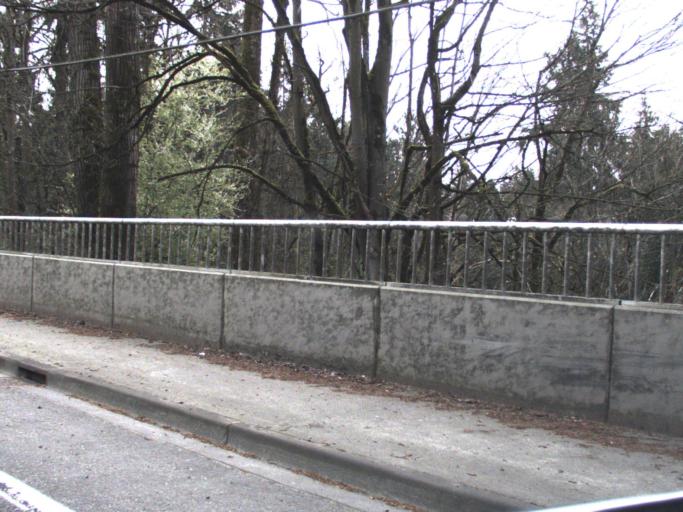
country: US
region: Washington
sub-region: King County
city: Kent
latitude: 47.3803
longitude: -122.2183
